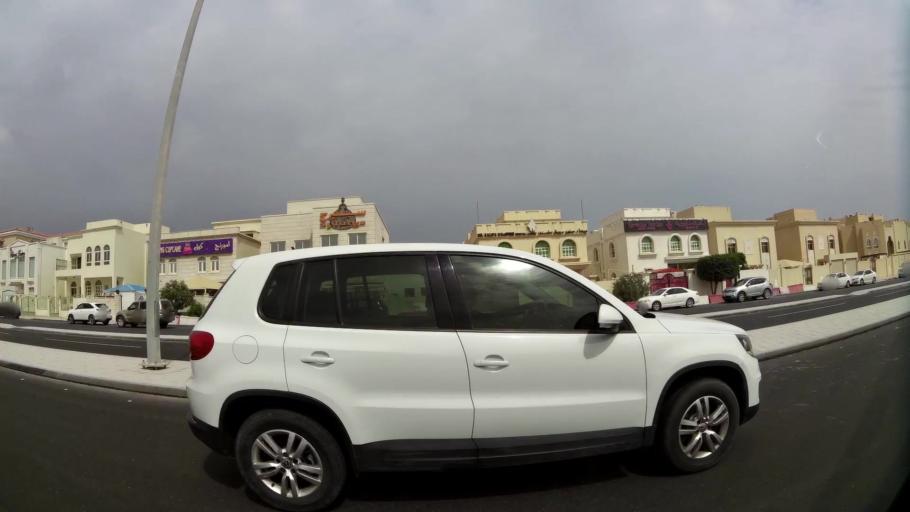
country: QA
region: Baladiyat ar Rayyan
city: Ar Rayyan
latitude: 25.3528
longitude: 51.4653
